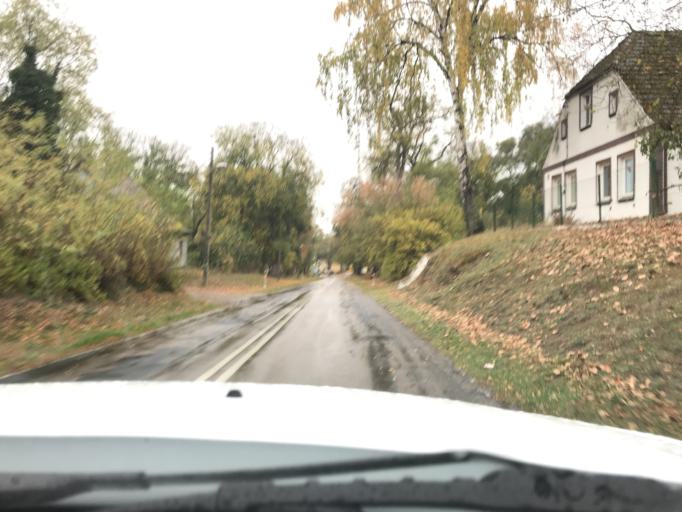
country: DE
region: Brandenburg
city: Neulewin
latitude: 52.7667
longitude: 14.3217
